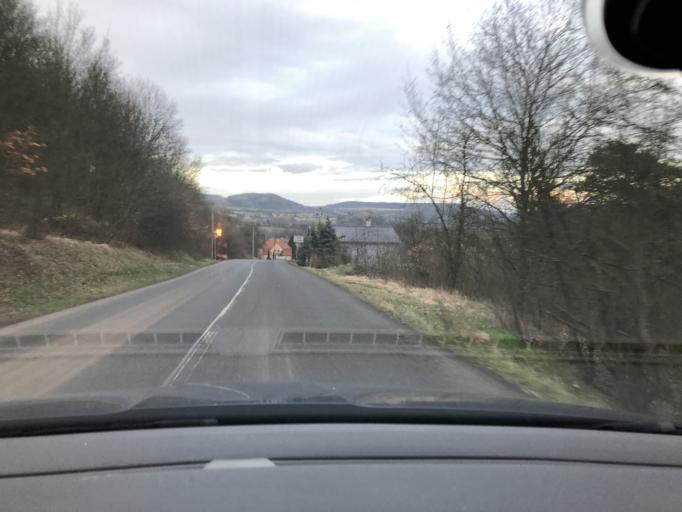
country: CZ
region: Ustecky
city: Rehlovice
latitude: 50.5984
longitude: 13.9082
